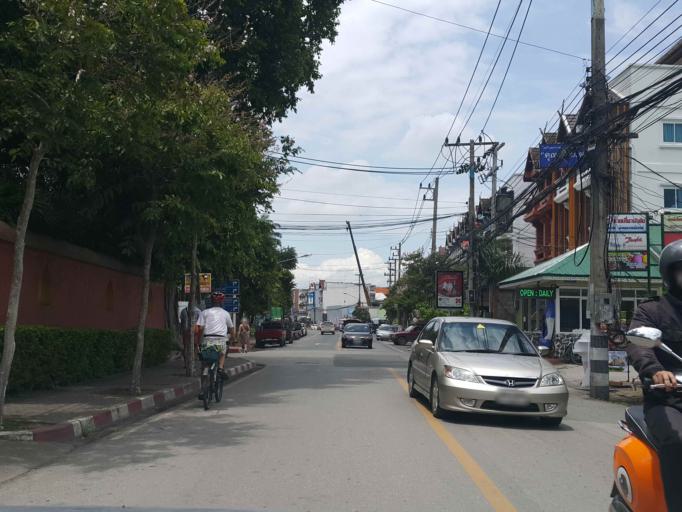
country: TH
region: Chiang Mai
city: Chiang Mai
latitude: 18.7874
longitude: 98.9824
